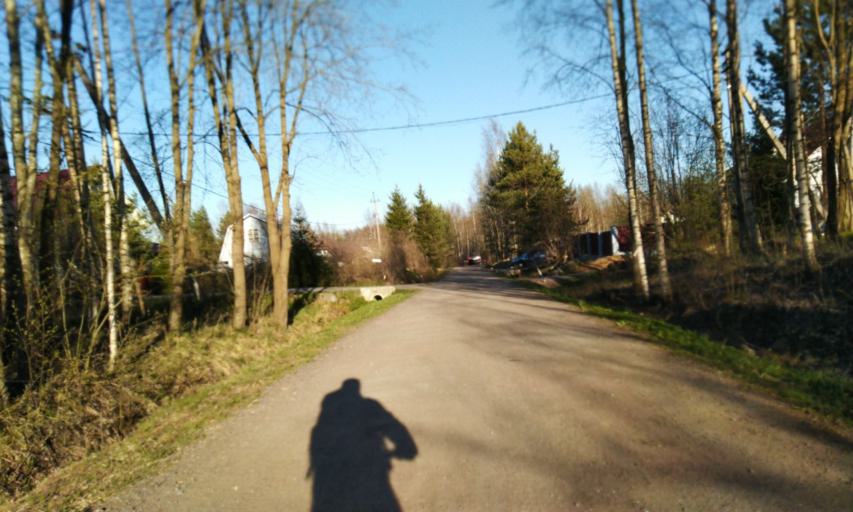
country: RU
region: Leningrad
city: Toksovo
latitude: 60.1521
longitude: 30.5800
